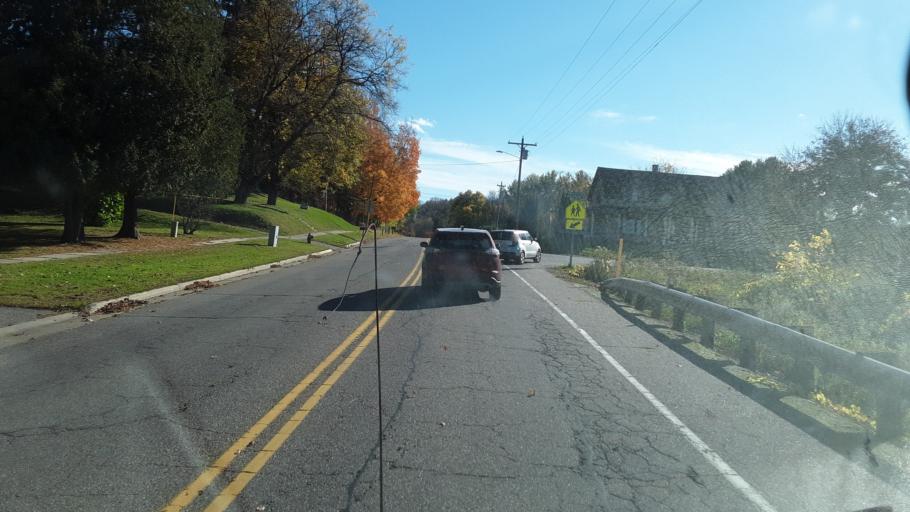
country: US
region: Wisconsin
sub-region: Sauk County
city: Reedsburg
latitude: 43.5802
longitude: -90.1343
